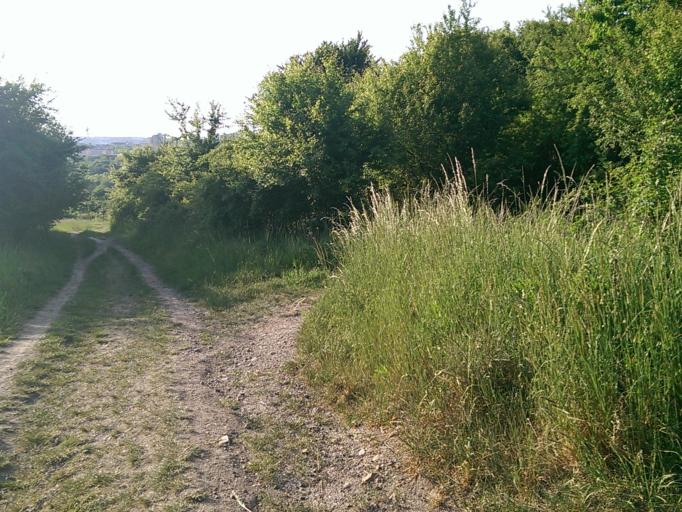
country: CZ
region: Central Bohemia
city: Vestec
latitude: 50.0446
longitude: 14.5023
